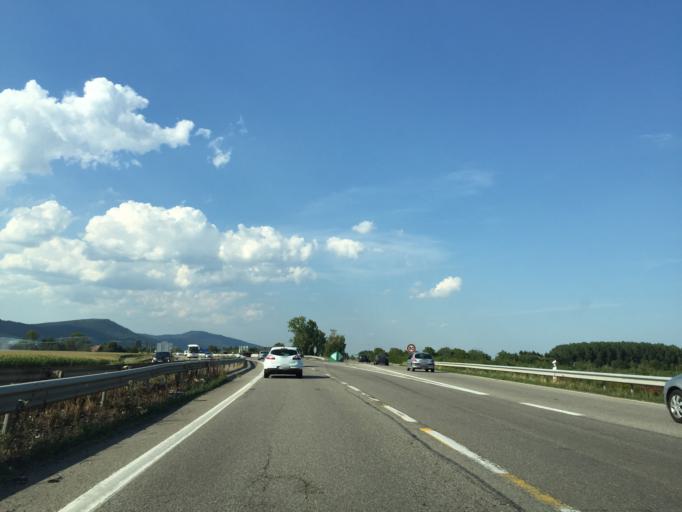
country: FR
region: Alsace
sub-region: Departement du Haut-Rhin
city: Guemar
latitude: 48.2116
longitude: 7.4018
